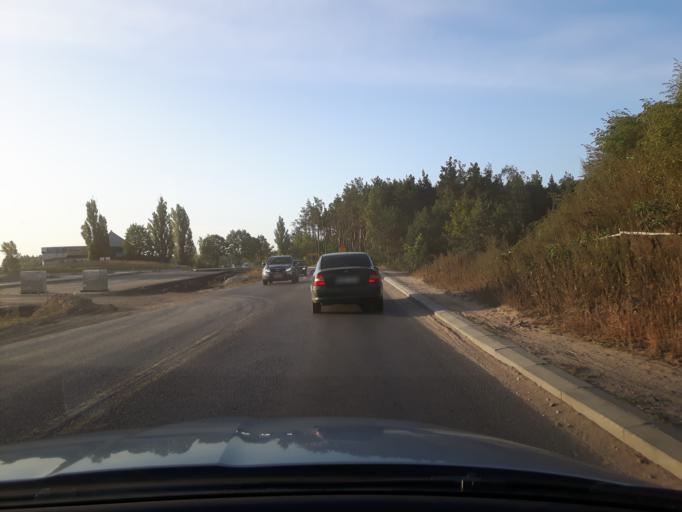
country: PL
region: Masovian Voivodeship
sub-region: Powiat piaseczynski
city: Gora Kalwaria
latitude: 51.9686
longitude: 21.2123
